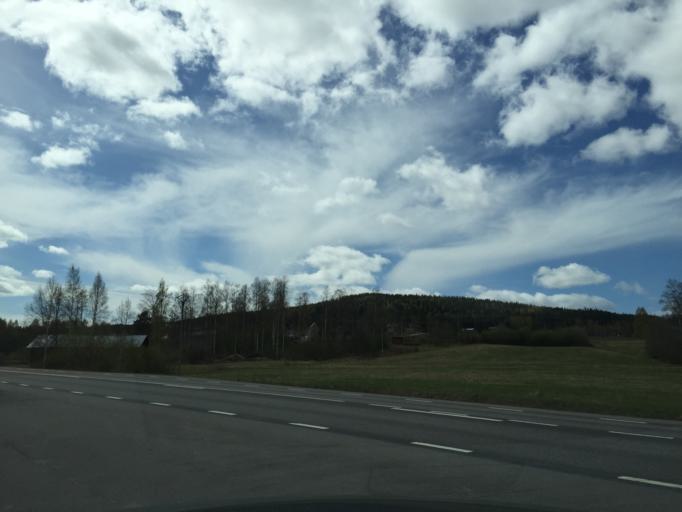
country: SE
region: Gaevleborg
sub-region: Bollnas Kommun
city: Arbra
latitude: 61.5041
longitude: 16.3574
